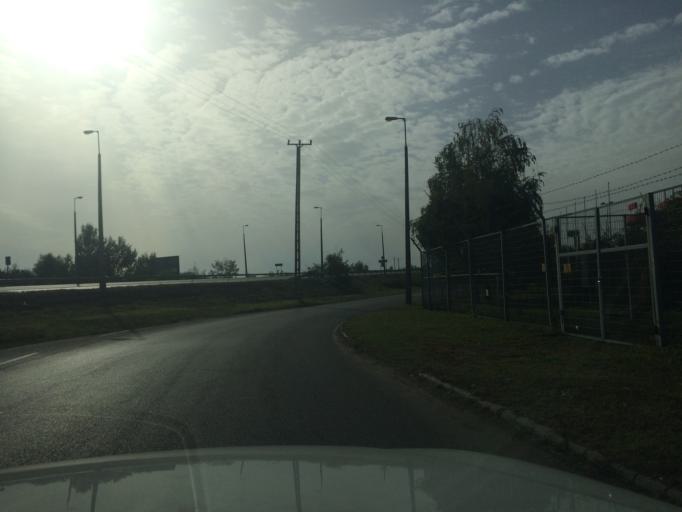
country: HU
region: Szabolcs-Szatmar-Bereg
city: Nyiregyhaza
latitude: 47.9185
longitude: 21.7190
